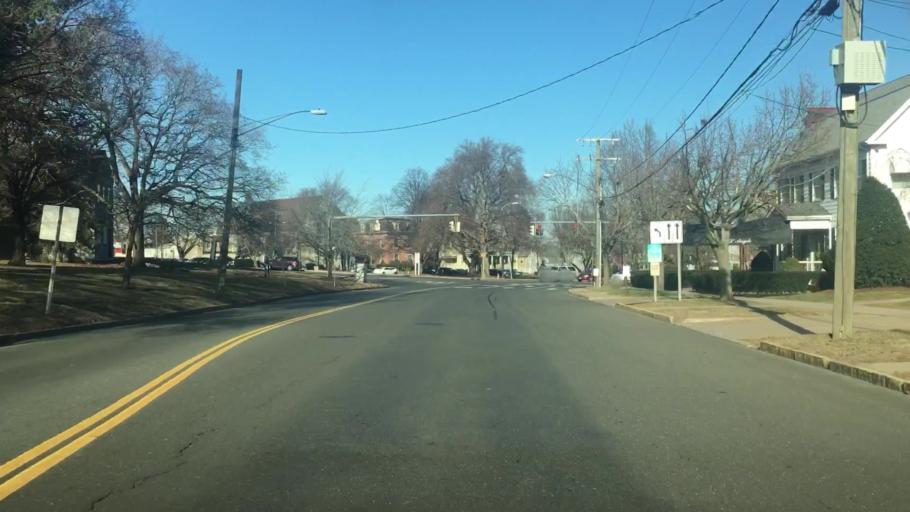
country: US
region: Connecticut
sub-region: Middlesex County
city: Middletown
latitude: 41.5552
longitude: -72.6487
